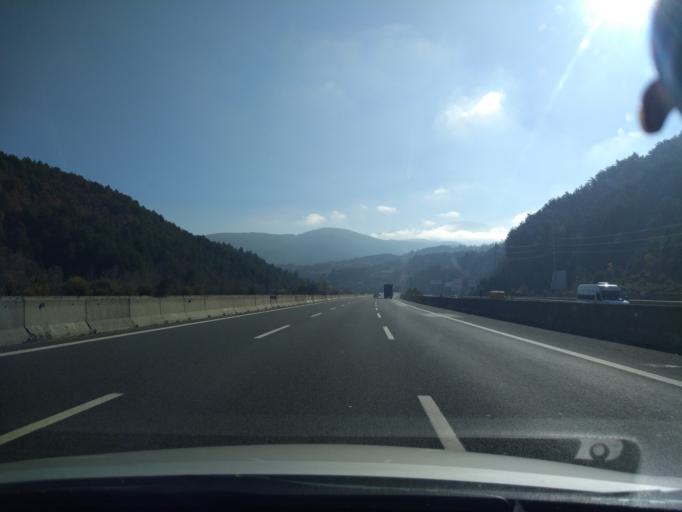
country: TR
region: Bolu
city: Bolu
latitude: 40.7479
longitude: 31.7803
